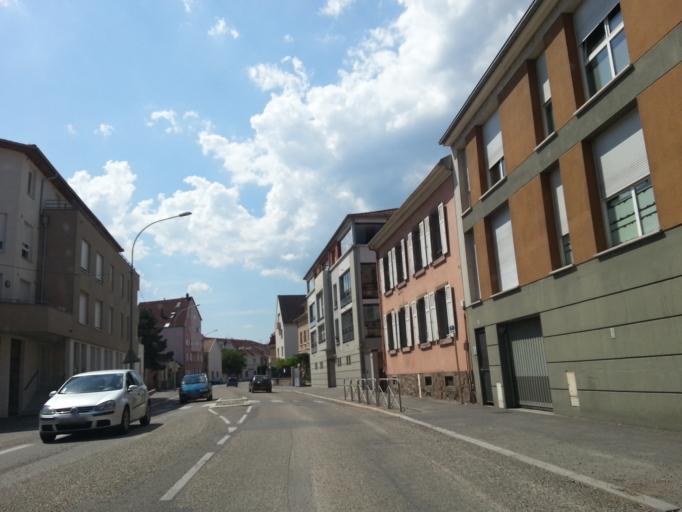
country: FR
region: Alsace
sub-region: Departement du Haut-Rhin
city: Colmar
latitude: 48.0801
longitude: 7.3676
